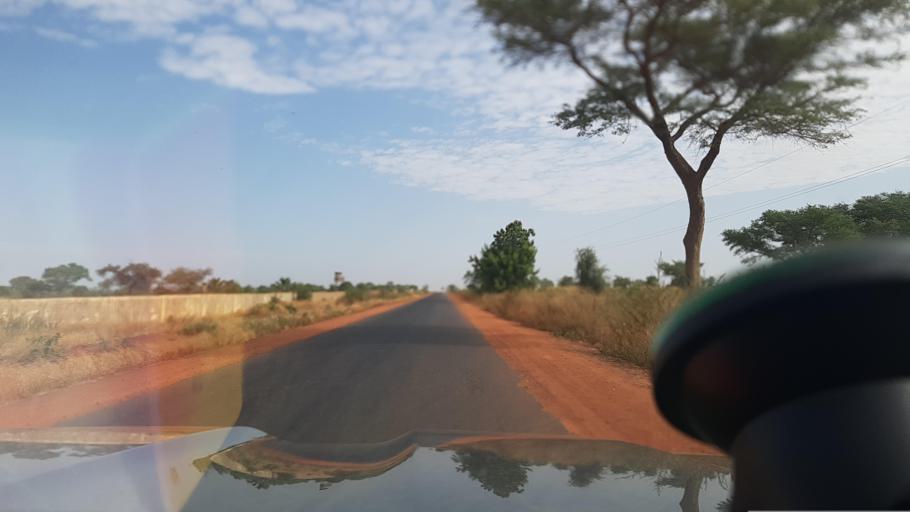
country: ML
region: Segou
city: Segou
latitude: 13.5336
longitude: -6.1253
